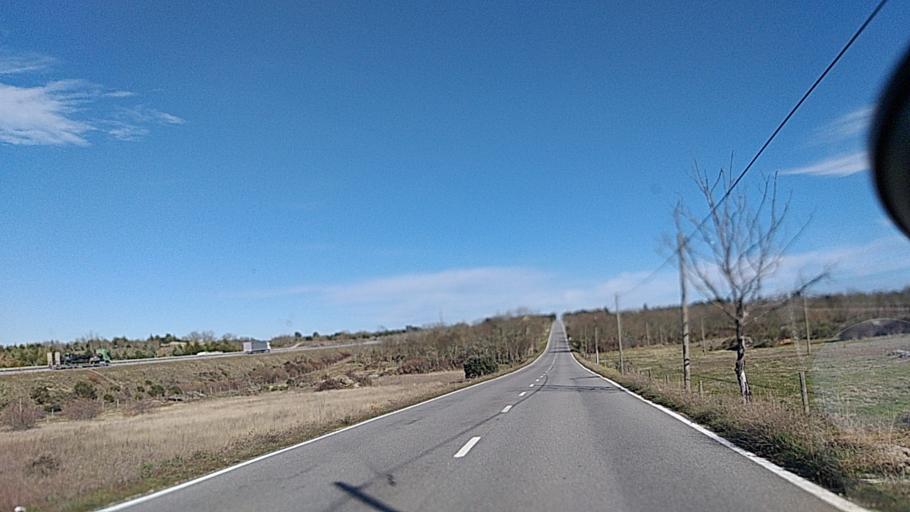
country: ES
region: Castille and Leon
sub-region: Provincia de Salamanca
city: Fuentes de Onoro
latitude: 40.6152
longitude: -6.8713
